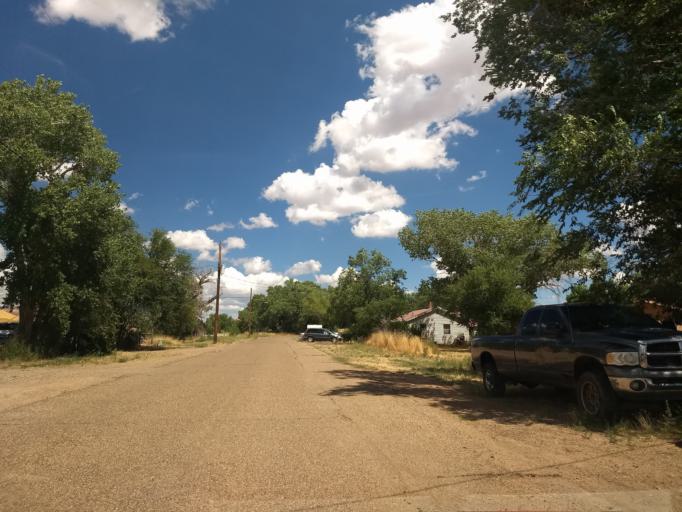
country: US
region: Arizona
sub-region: Coconino County
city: Fredonia
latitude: 36.9478
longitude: -112.5307
